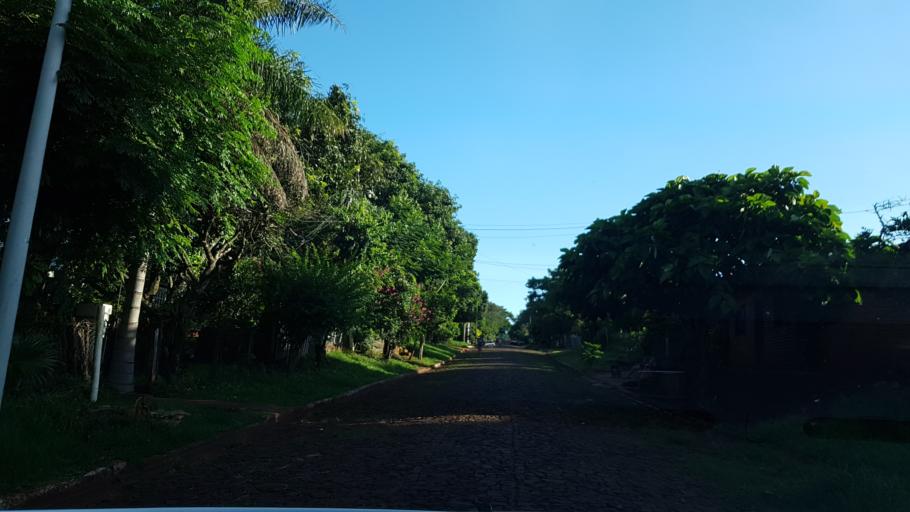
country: AR
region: Misiones
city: Puerto Libertad
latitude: -25.9183
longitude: -54.5868
